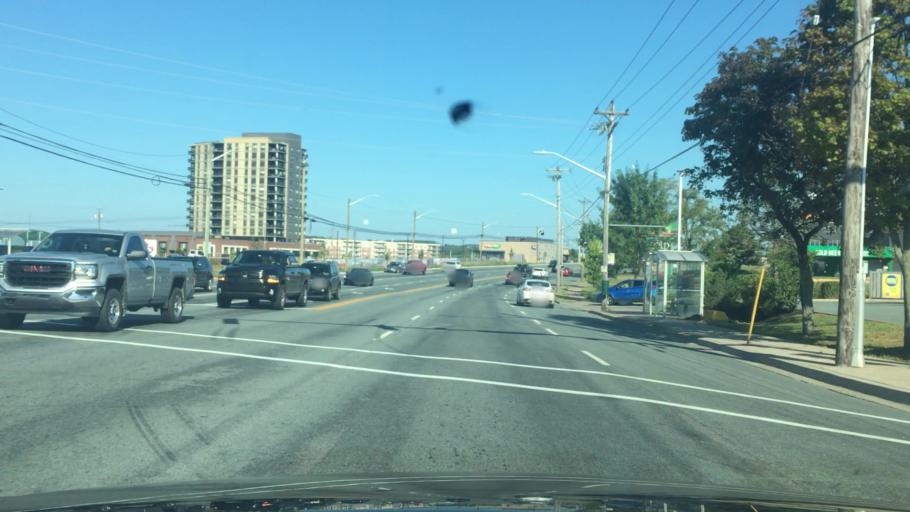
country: CA
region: Nova Scotia
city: Dartmouth
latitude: 44.6984
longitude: -63.6049
